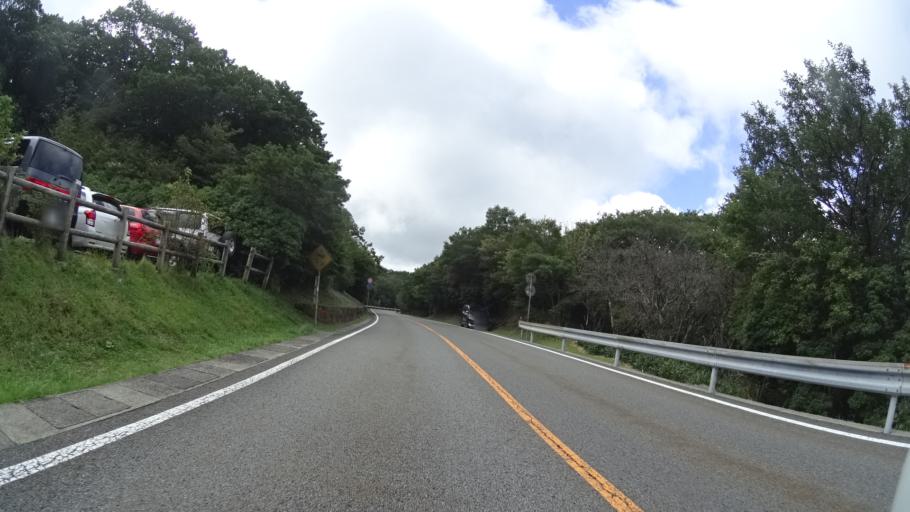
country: JP
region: Oita
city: Tsukawaki
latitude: 33.0952
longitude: 131.2068
